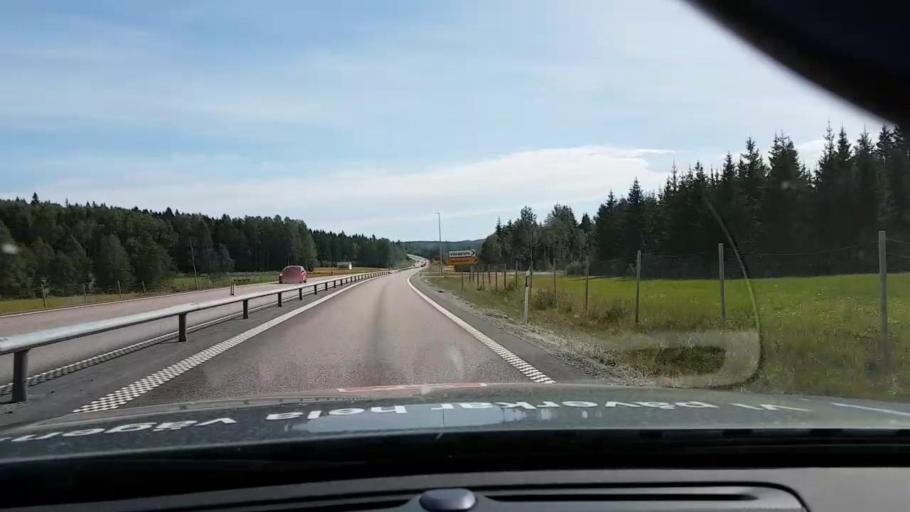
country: SE
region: Vaesternorrland
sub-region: OErnskoeldsviks Kommun
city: Ornskoldsvik
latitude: 63.3030
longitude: 18.8576
